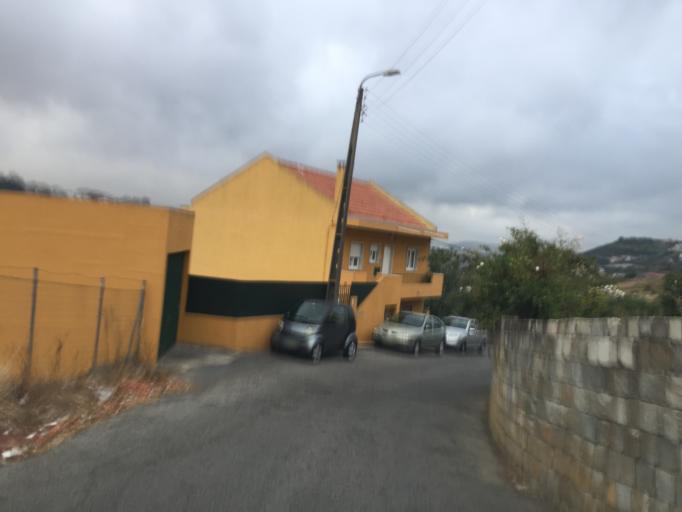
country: PT
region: Lisbon
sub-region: Odivelas
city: Olival do Basto
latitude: 38.7955
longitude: -9.1562
